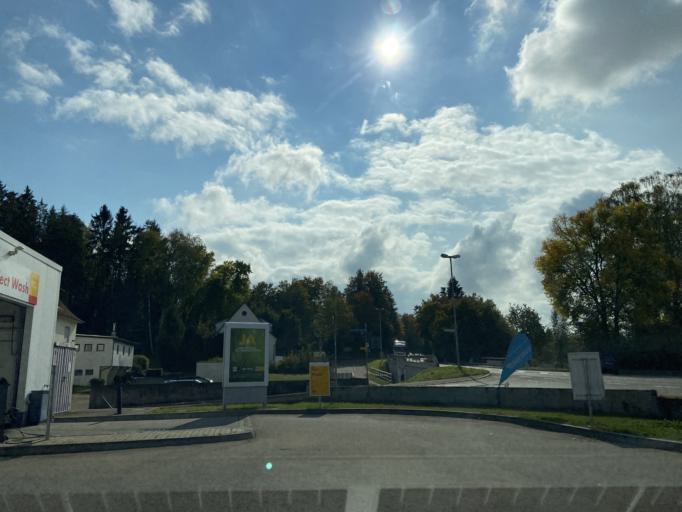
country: DE
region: Baden-Wuerttemberg
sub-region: Tuebingen Region
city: Sigmaringen
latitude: 48.0880
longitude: 9.2300
